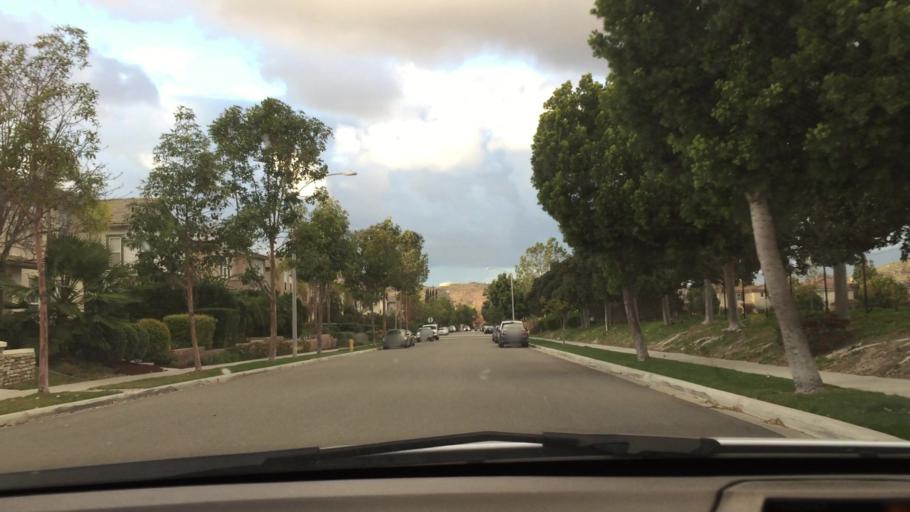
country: US
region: California
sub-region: San Diego County
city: Fairbanks Ranch
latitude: 33.0135
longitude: -117.1149
